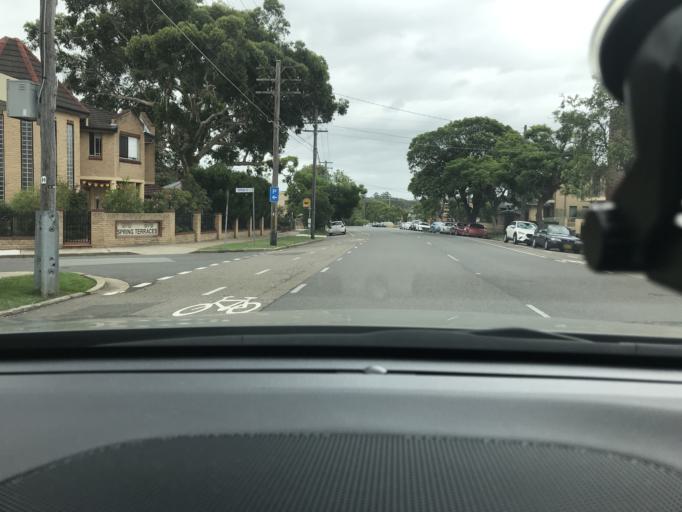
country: AU
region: New South Wales
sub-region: Canada Bay
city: Wareemba
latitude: -33.8473
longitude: 151.1283
